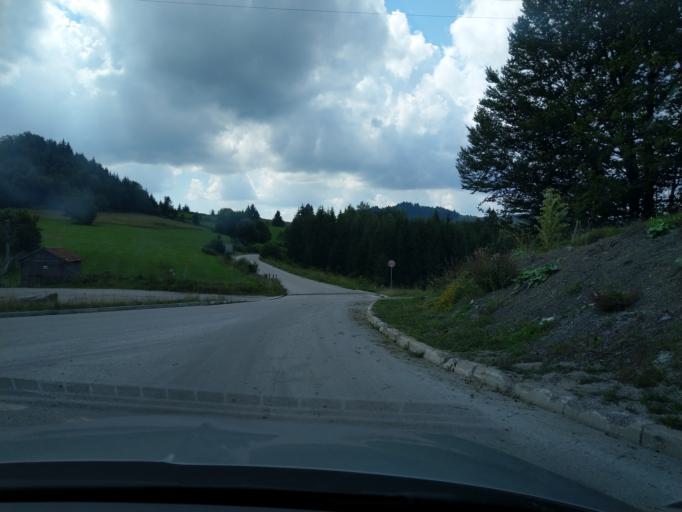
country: RS
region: Central Serbia
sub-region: Zlatiborski Okrug
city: Nova Varos
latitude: 43.5576
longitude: 19.8992
